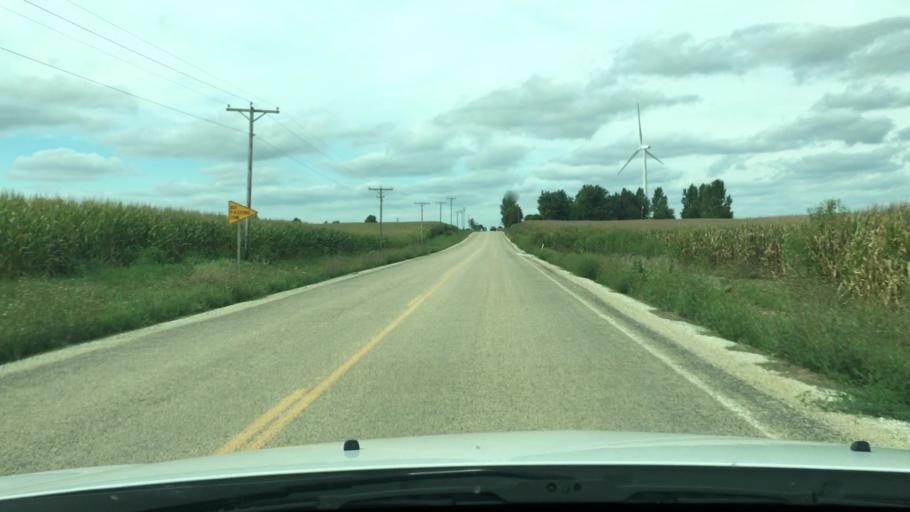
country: US
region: Illinois
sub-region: DeKalb County
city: Waterman
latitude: 41.8167
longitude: -88.7733
